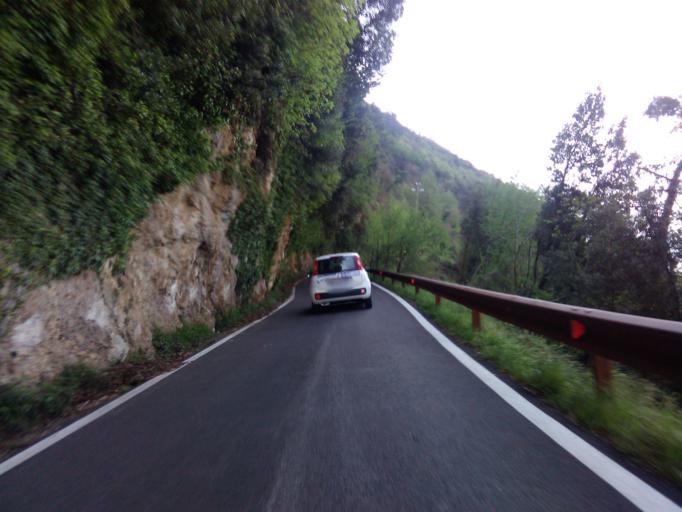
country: IT
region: Tuscany
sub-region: Provincia di Lucca
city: Pontestazzemese
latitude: 43.9629
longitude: 10.2789
